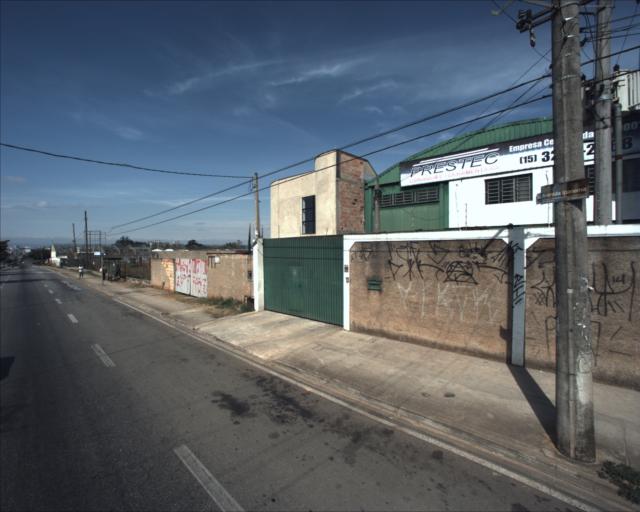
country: BR
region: Sao Paulo
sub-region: Sorocaba
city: Sorocaba
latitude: -23.4556
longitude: -47.5050
